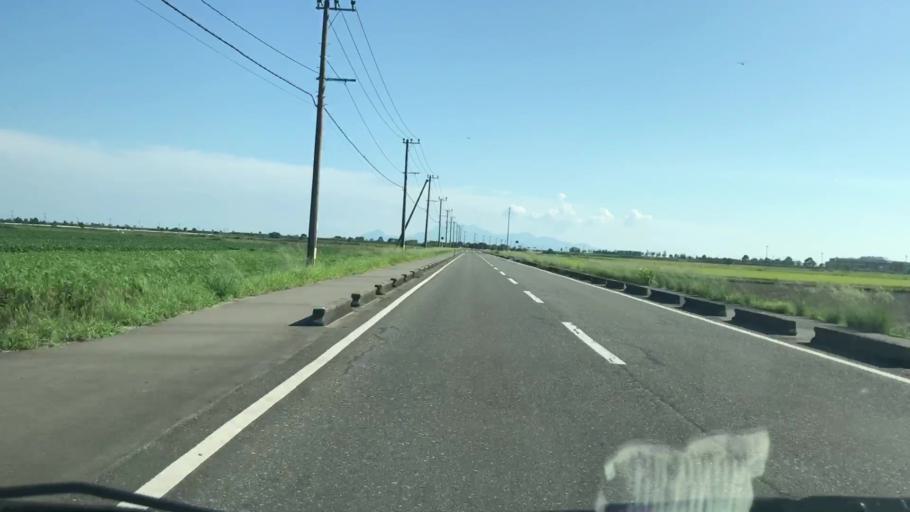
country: JP
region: Saga Prefecture
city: Okawa
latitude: 33.1629
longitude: 130.3088
